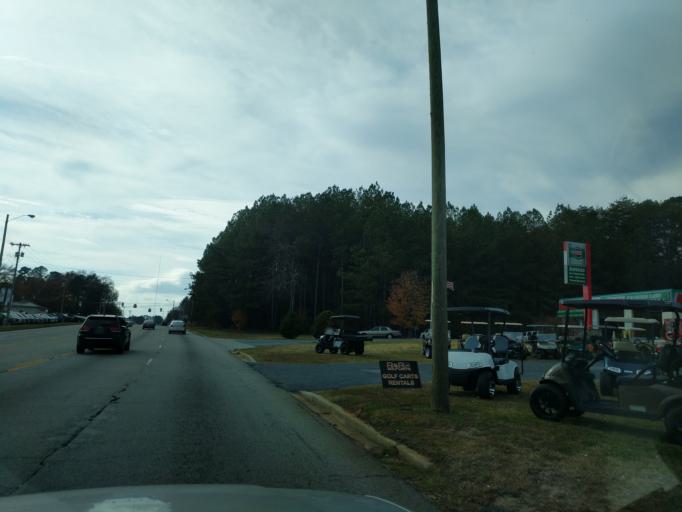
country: US
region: South Carolina
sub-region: Oconee County
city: Seneca
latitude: 34.6976
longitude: -82.9654
